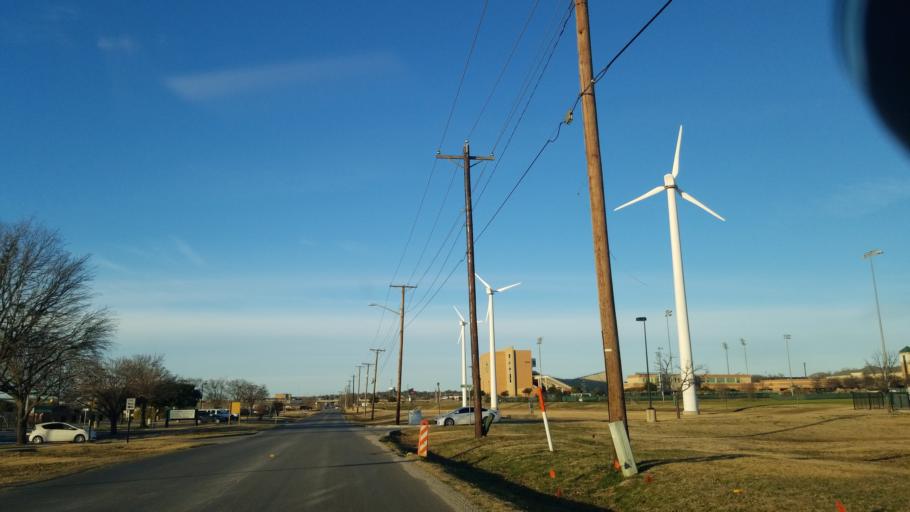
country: US
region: Texas
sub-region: Denton County
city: Denton
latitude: 33.1991
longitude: -97.1615
